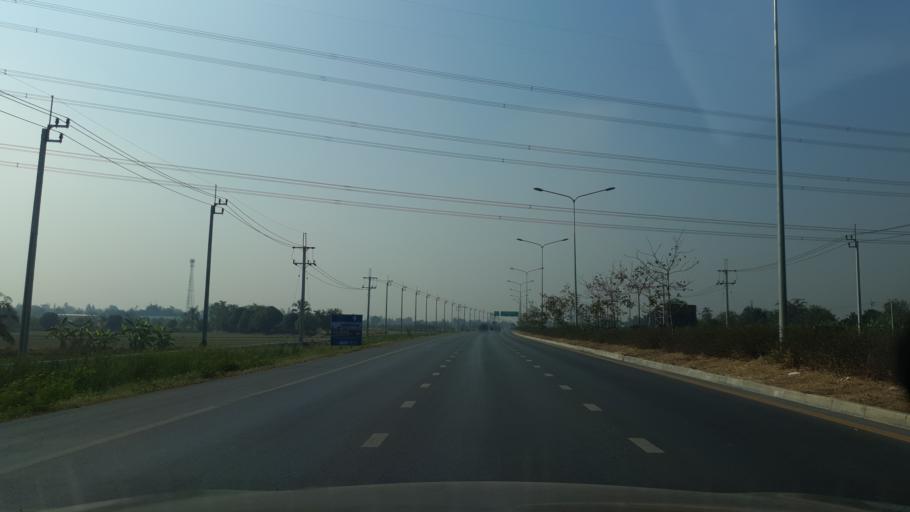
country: TH
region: Nonthaburi
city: Bang Bua Thong
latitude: 13.9701
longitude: 100.4632
